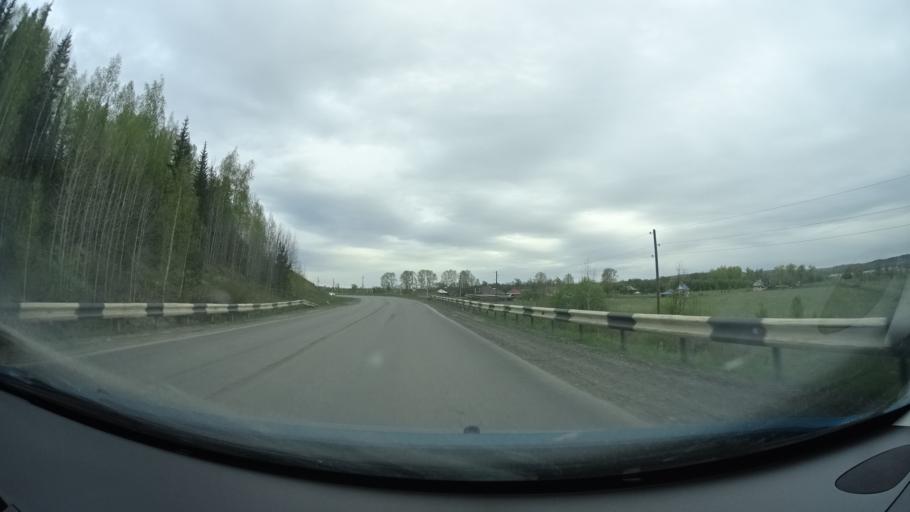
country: RU
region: Perm
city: Osa
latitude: 57.2070
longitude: 55.5887
